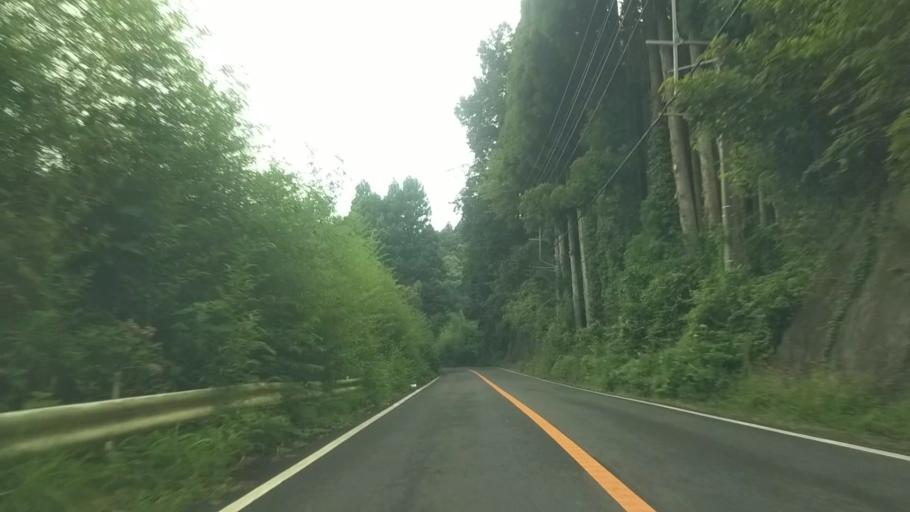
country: JP
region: Chiba
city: Kawaguchi
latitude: 35.2341
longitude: 140.0728
